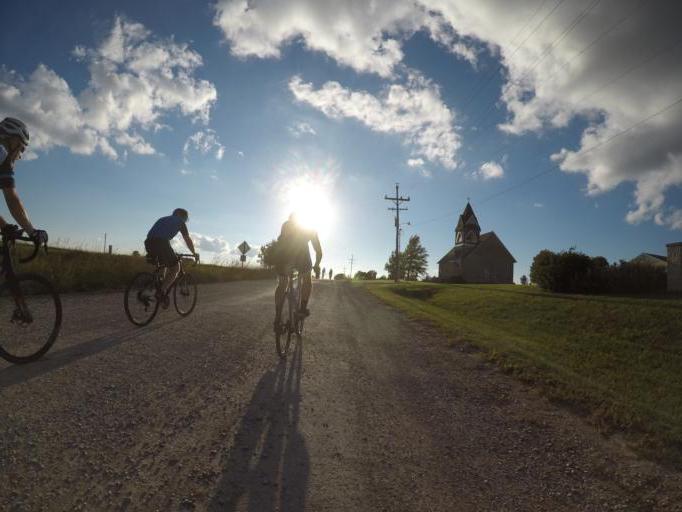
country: US
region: Kansas
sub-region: Riley County
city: Manhattan
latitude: 39.2616
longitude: -96.6827
